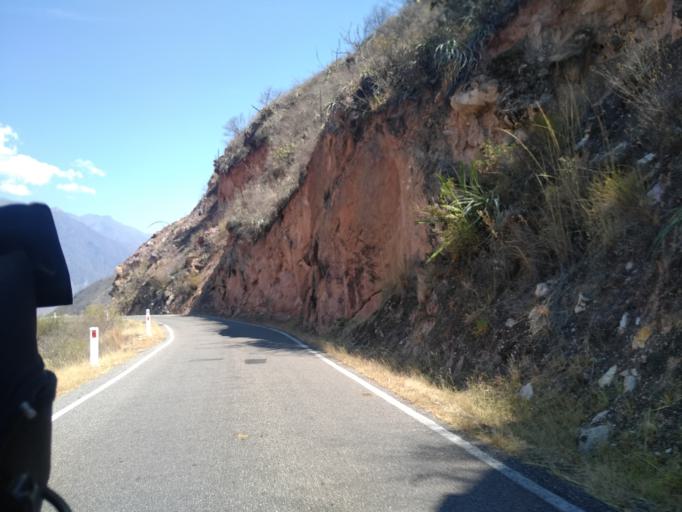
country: PE
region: Amazonas
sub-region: Provincia de Chachapoyas
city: Balsas
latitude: -6.8486
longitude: -77.9848
